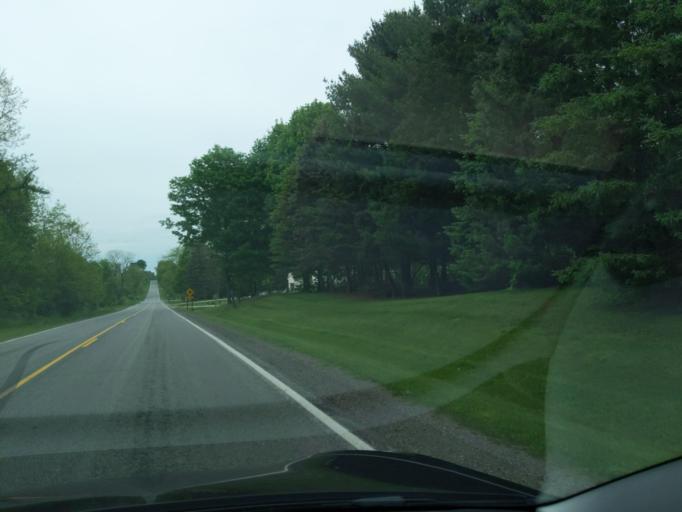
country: US
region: Michigan
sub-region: Ingham County
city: Leslie
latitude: 42.4475
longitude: -84.3908
